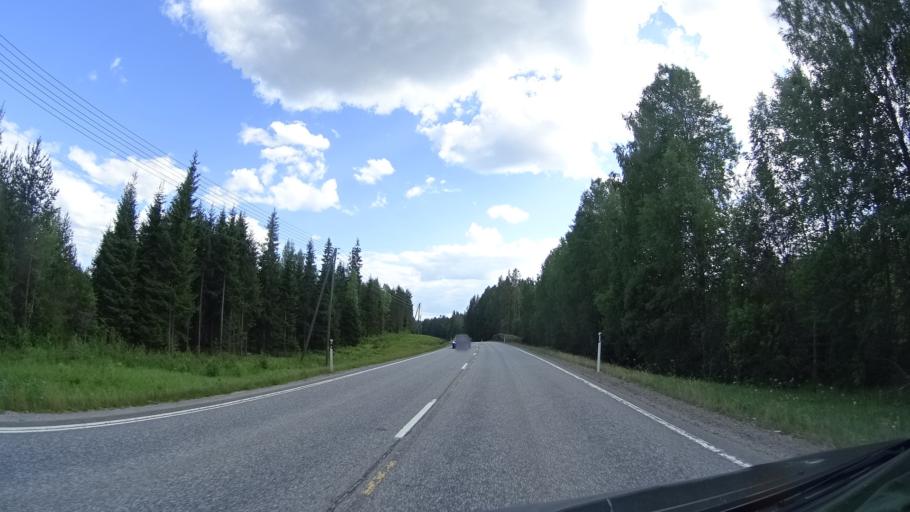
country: FI
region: Southern Savonia
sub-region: Savonlinna
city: Punkaharju
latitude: 61.6691
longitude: 29.4121
